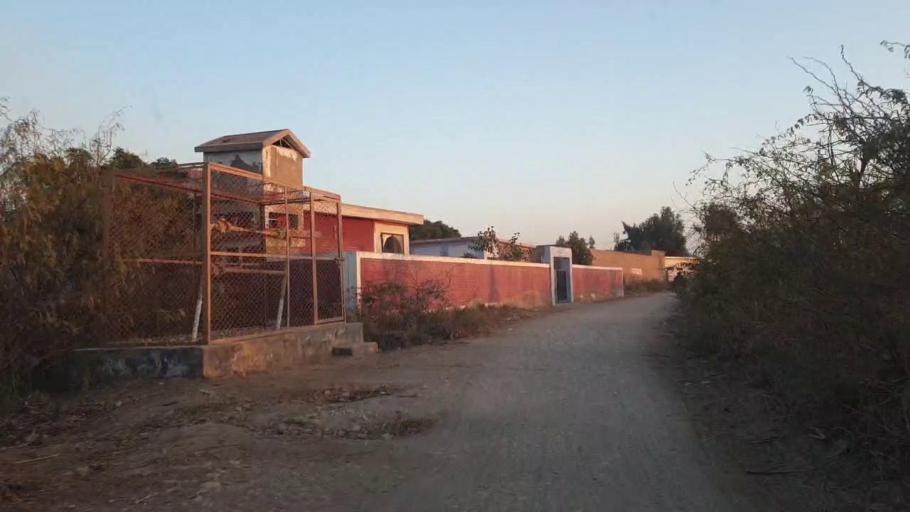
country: PK
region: Sindh
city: Chambar
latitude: 25.3555
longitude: 68.7491
